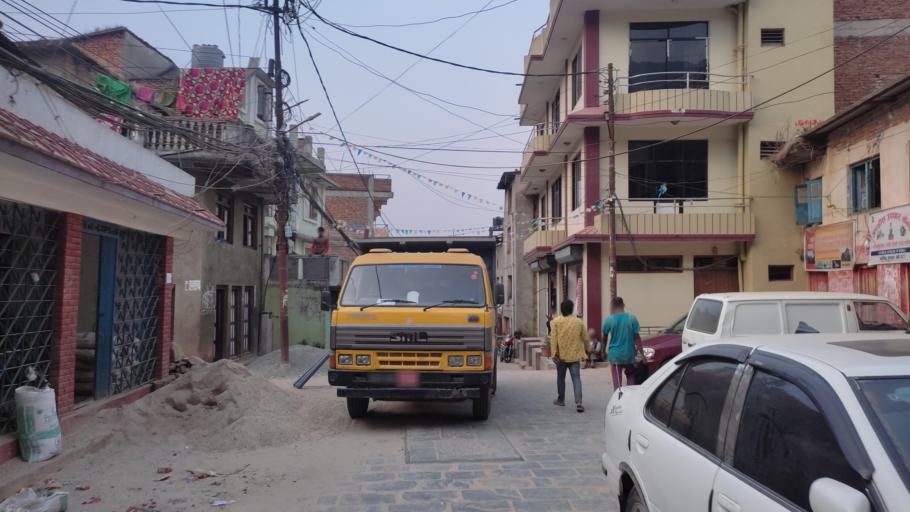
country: NP
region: Central Region
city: Kirtipur
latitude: 27.6684
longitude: 85.2493
